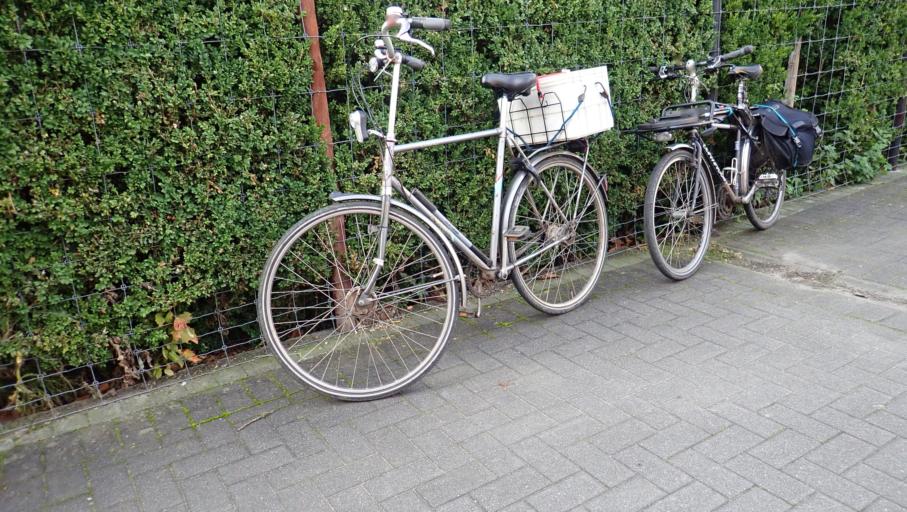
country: BE
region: Flanders
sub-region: Provincie Oost-Vlaanderen
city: Stekene
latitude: 51.1578
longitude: 4.0421
